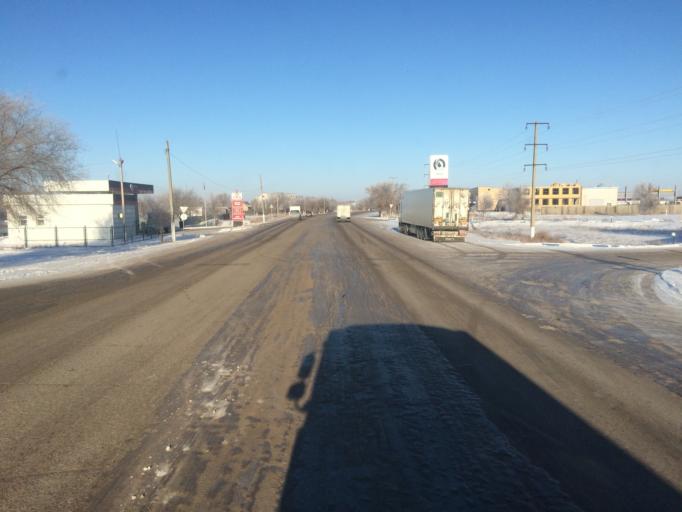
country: KZ
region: Aqtoebe
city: Aqtobe
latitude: 50.2462
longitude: 57.2506
